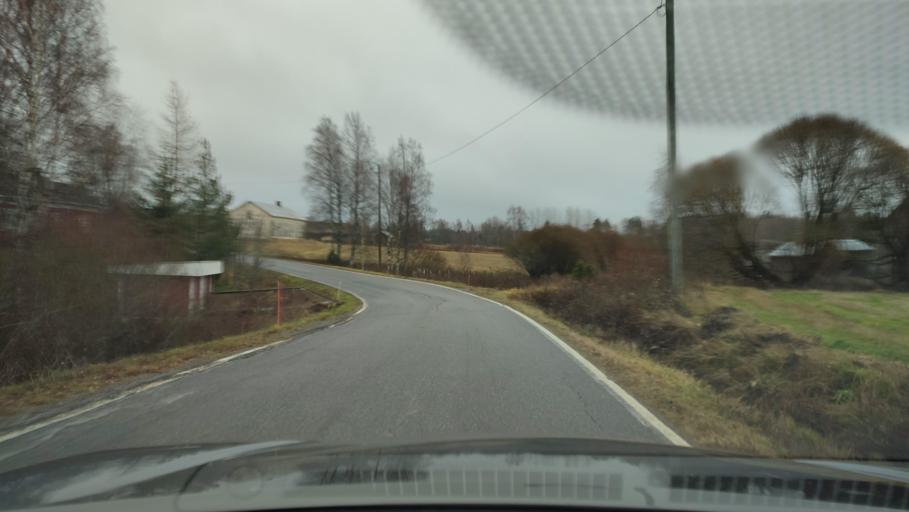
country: FI
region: Southern Ostrobothnia
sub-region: Suupohja
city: Isojoki
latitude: 62.1807
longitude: 21.9141
